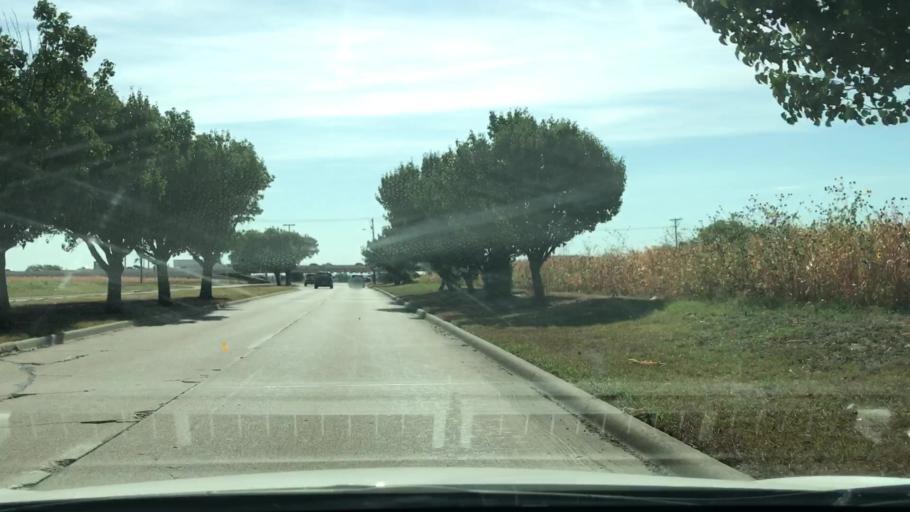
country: US
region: Texas
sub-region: Collin County
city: McKinney
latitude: 33.2291
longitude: -96.6369
